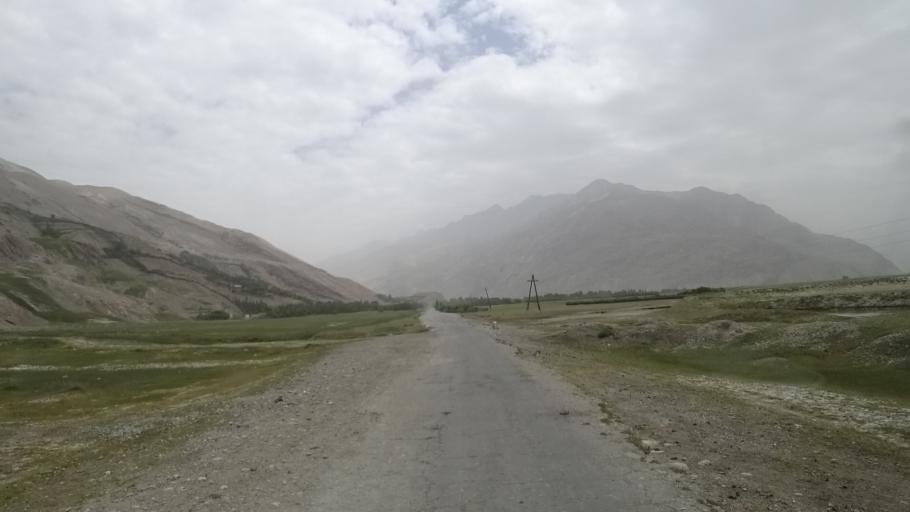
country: AF
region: Badakhshan
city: Khandud
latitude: 37.0331
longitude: 72.6357
